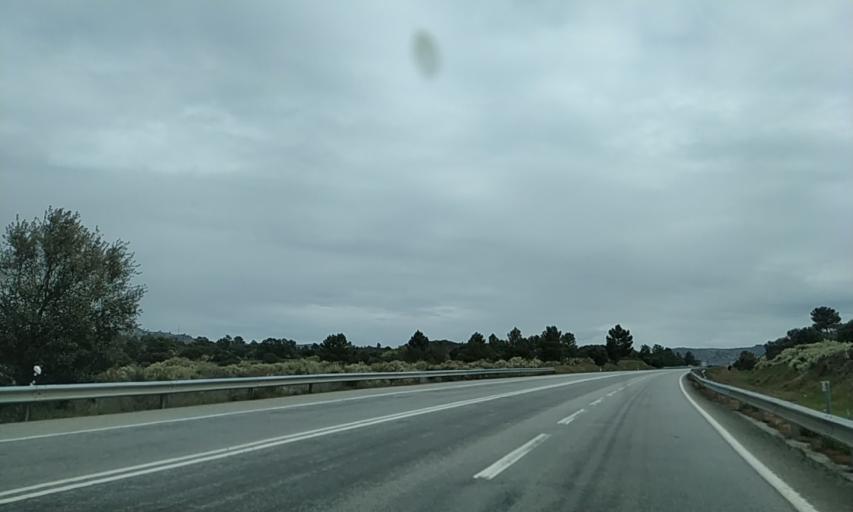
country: PT
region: Guarda
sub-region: Celorico da Beira
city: Celorico da Beira
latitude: 40.6343
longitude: -7.3165
